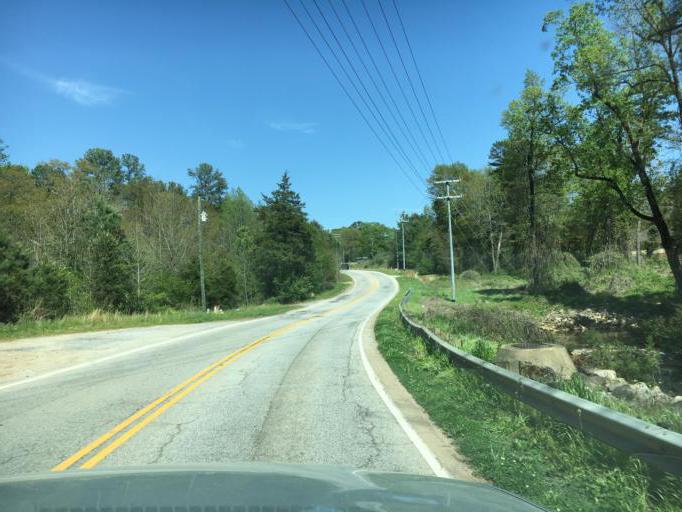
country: US
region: South Carolina
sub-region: Greenville County
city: Greer
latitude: 34.9600
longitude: -82.2294
